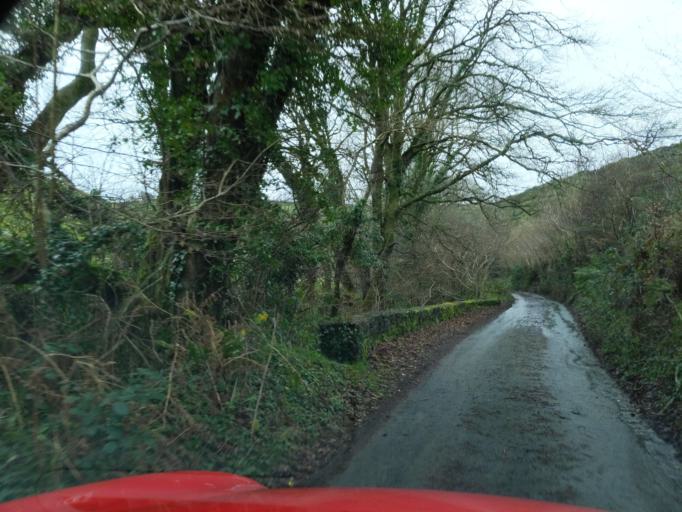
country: GB
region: England
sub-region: Cornwall
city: Duloe
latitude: 50.3472
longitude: -4.5188
